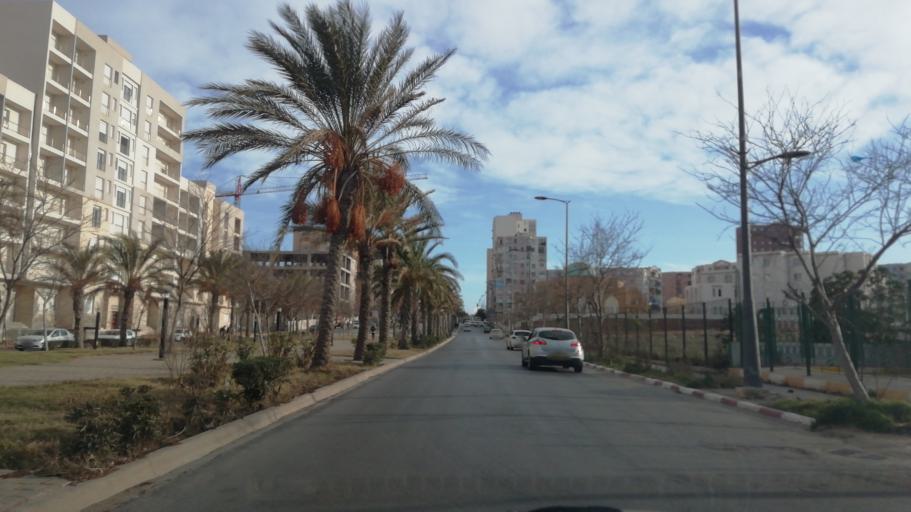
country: DZ
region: Oran
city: Bir el Djir
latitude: 35.7247
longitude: -0.5937
